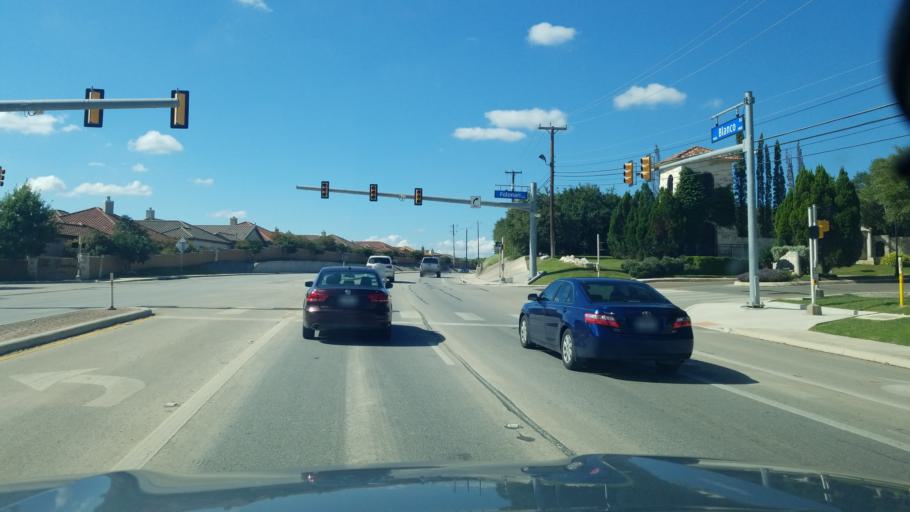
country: US
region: Texas
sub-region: Bexar County
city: Hollywood Park
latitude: 29.6234
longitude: -98.5167
